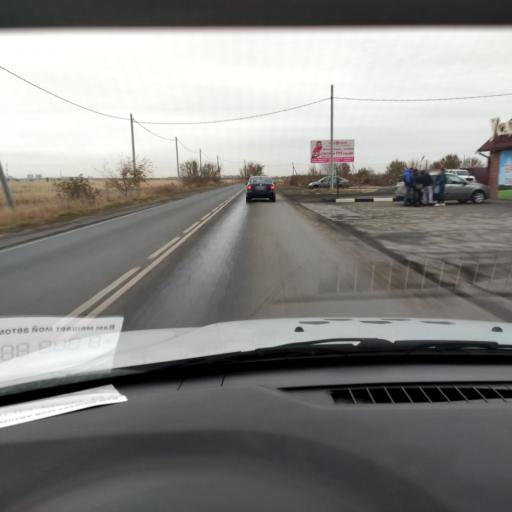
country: RU
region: Samara
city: Podstepki
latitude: 53.5191
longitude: 49.2213
